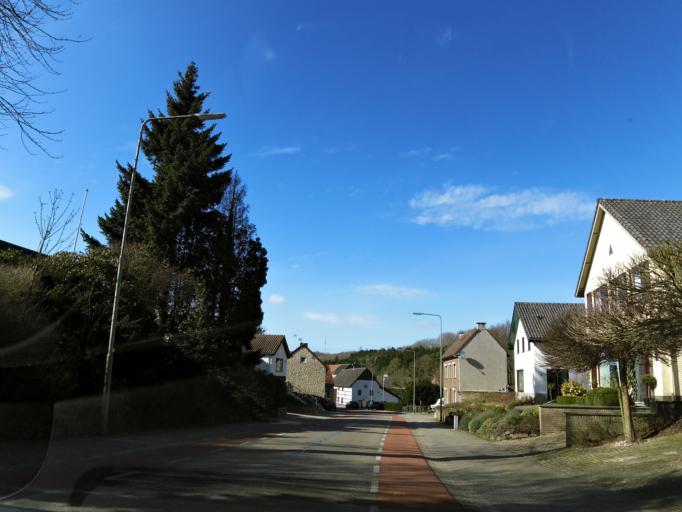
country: NL
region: Limburg
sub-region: Gemeente Voerendaal
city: Ubachsberg
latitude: 50.8242
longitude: 5.9487
